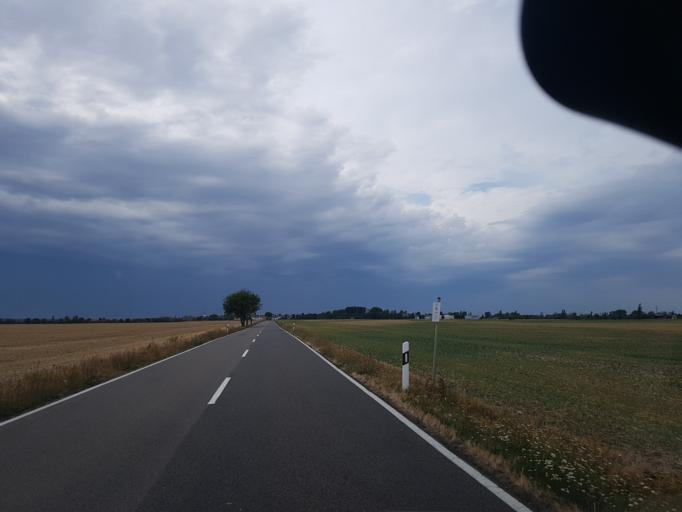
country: DE
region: Saxony
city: Strehla
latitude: 51.3953
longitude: 13.2689
